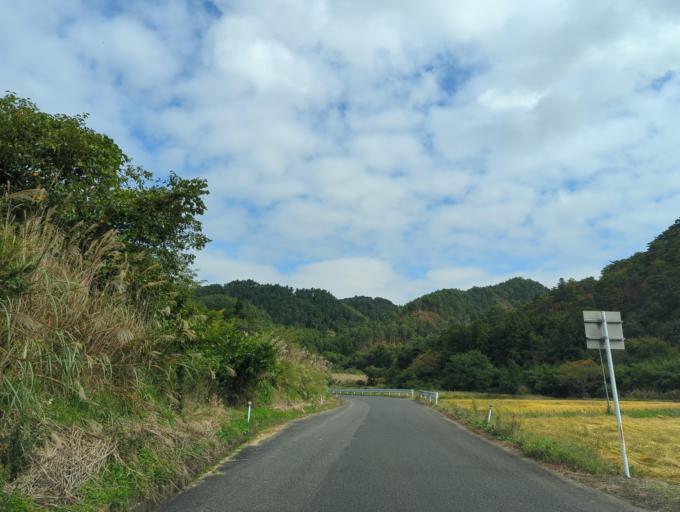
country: JP
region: Fukushima
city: Motomiya
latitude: 37.5061
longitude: 140.3258
